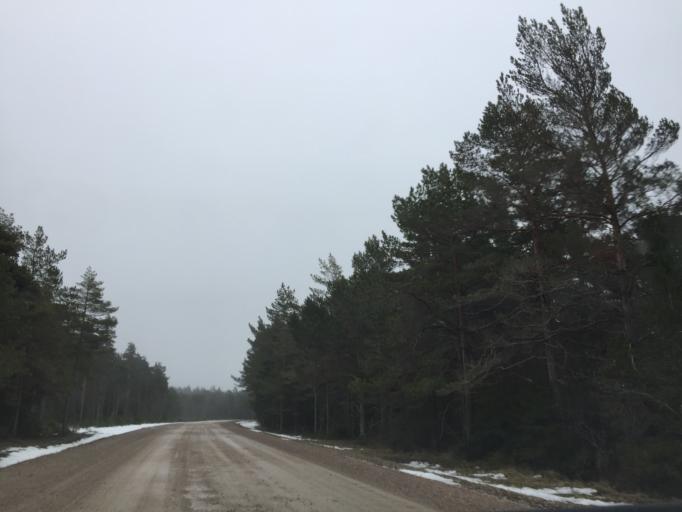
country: EE
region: Saare
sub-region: Kuressaare linn
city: Kuressaare
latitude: 58.4872
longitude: 21.9918
